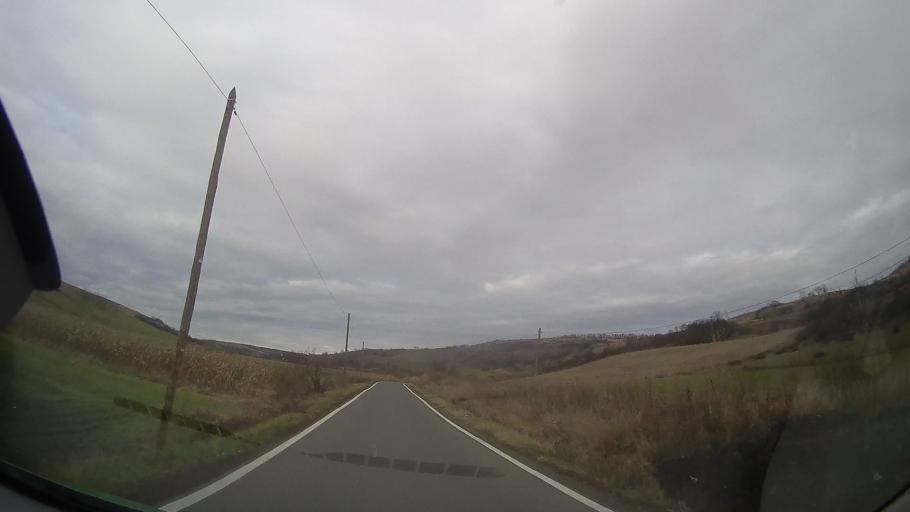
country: RO
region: Mures
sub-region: Comuna Cozma
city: Cozma
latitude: 46.7990
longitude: 24.5376
